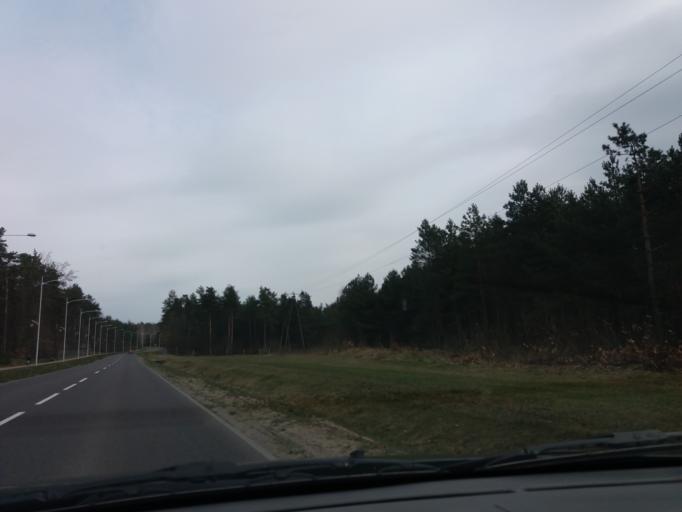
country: PL
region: Masovian Voivodeship
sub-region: Powiat mlawski
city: Mlawa
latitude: 53.1309
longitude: 20.3892
